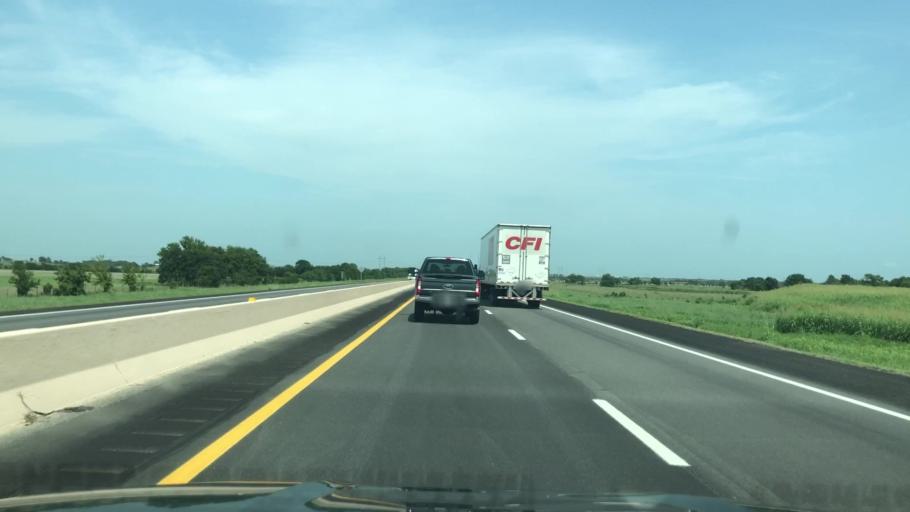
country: US
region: Oklahoma
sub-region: Craig County
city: Vinita
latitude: 36.6705
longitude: -95.0673
